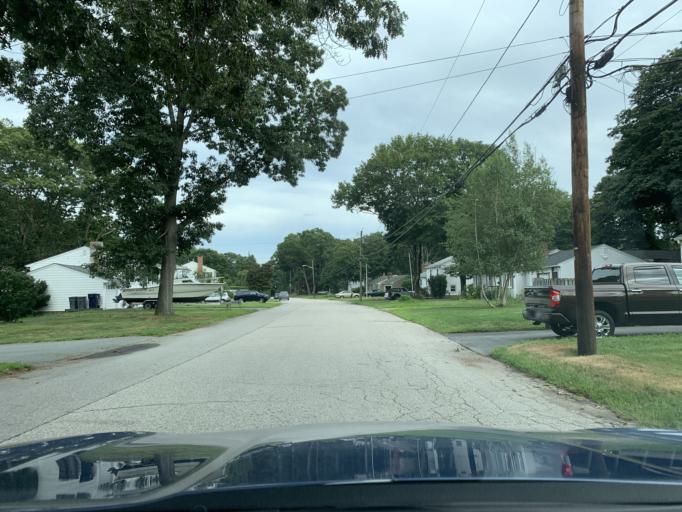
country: US
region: Rhode Island
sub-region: Kent County
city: East Greenwich
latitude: 41.6122
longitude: -71.4703
